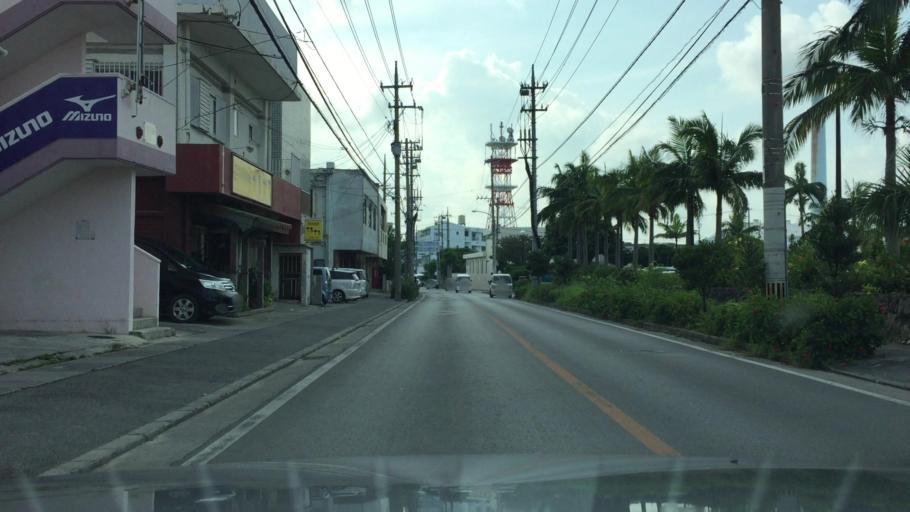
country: JP
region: Okinawa
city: Ishigaki
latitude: 24.3468
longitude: 124.1608
